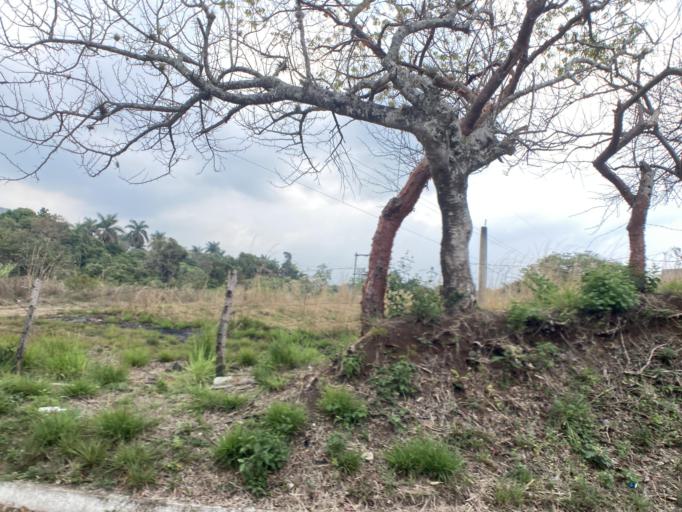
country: GT
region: Guatemala
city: Fraijanes
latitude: 14.3972
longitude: -90.4809
